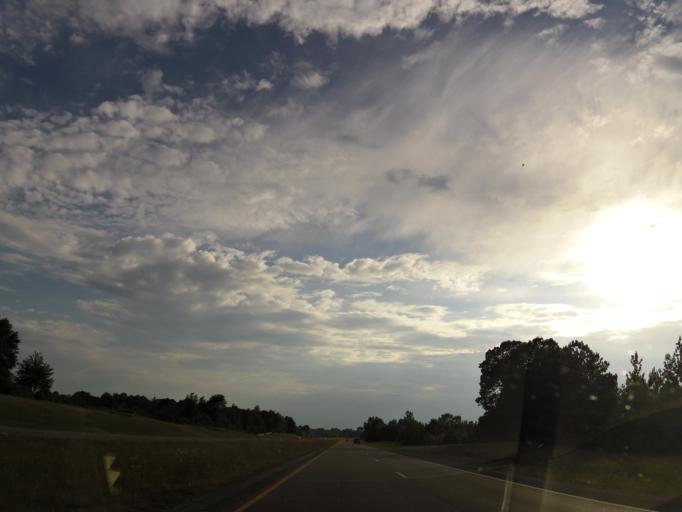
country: US
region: Alabama
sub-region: Morgan County
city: Trinity
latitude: 34.5366
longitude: -87.1639
